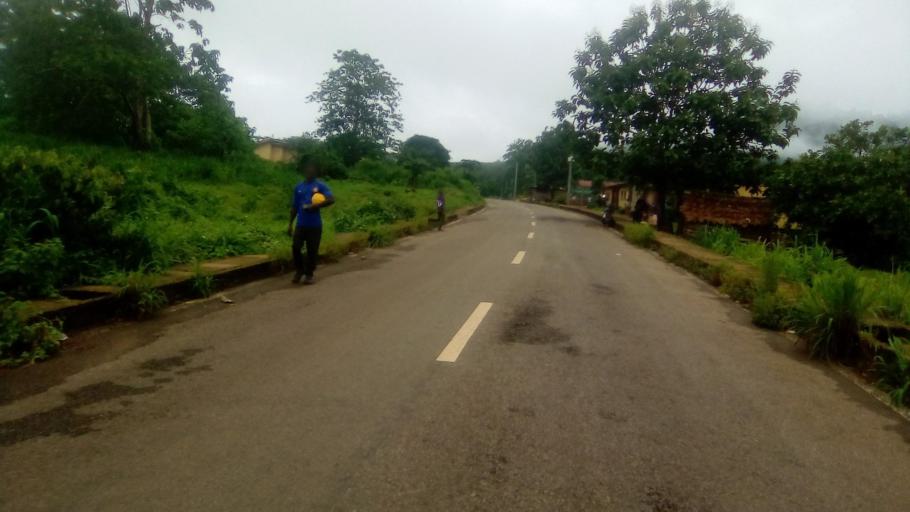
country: SL
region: Southern Province
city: Moyamba
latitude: 8.1630
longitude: -12.4467
